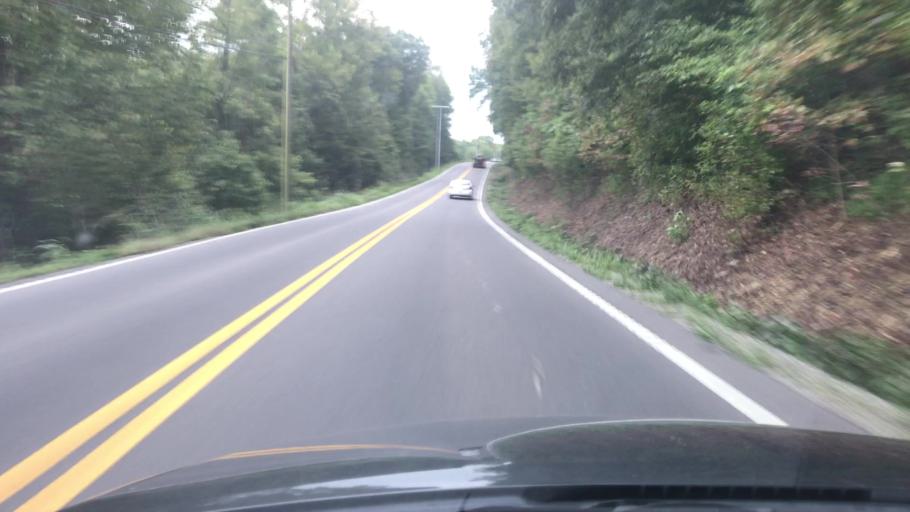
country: US
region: Tennessee
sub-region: Cheatham County
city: Ashland City
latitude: 36.2781
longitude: -87.0960
